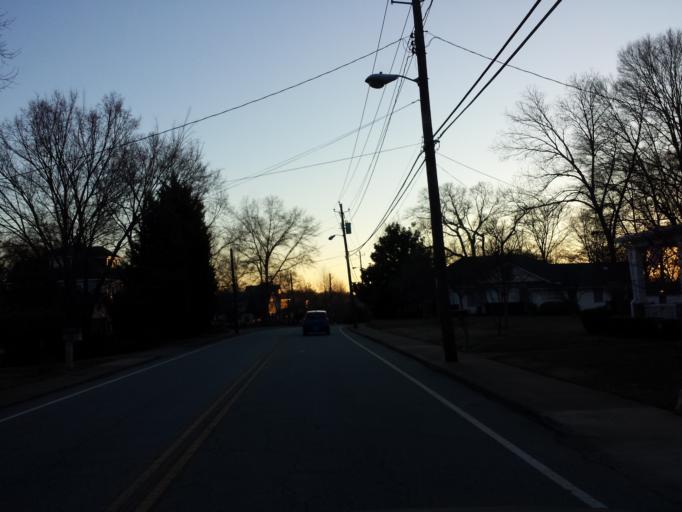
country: US
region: Georgia
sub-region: Cobb County
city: Smyrna
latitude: 33.8866
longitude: -84.5127
